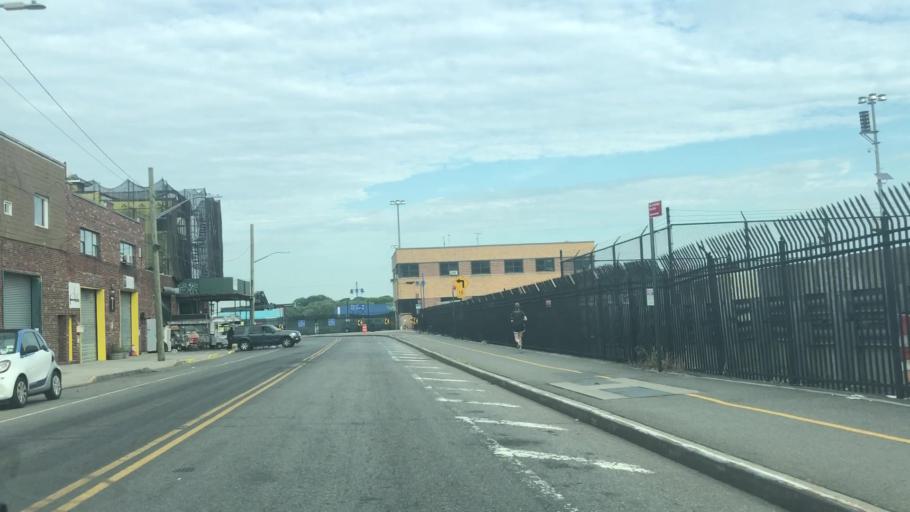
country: US
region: New York
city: New York City
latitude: 40.6861
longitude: -74.0034
